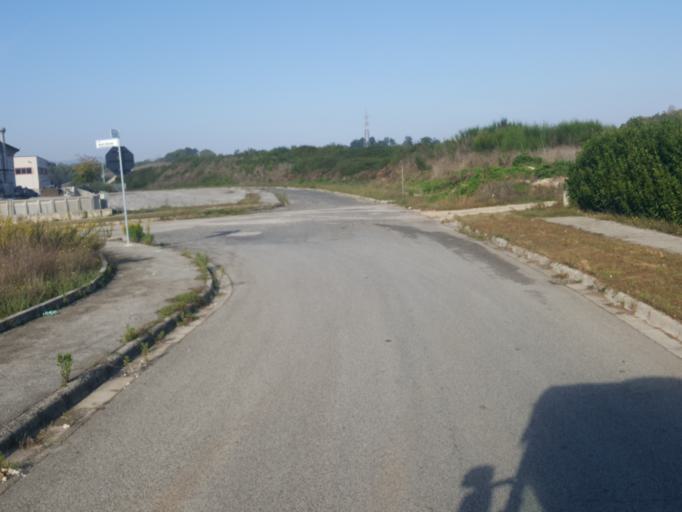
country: IT
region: Latium
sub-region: Citta metropolitana di Roma Capitale
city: Colleferro
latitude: 41.7576
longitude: 12.9912
